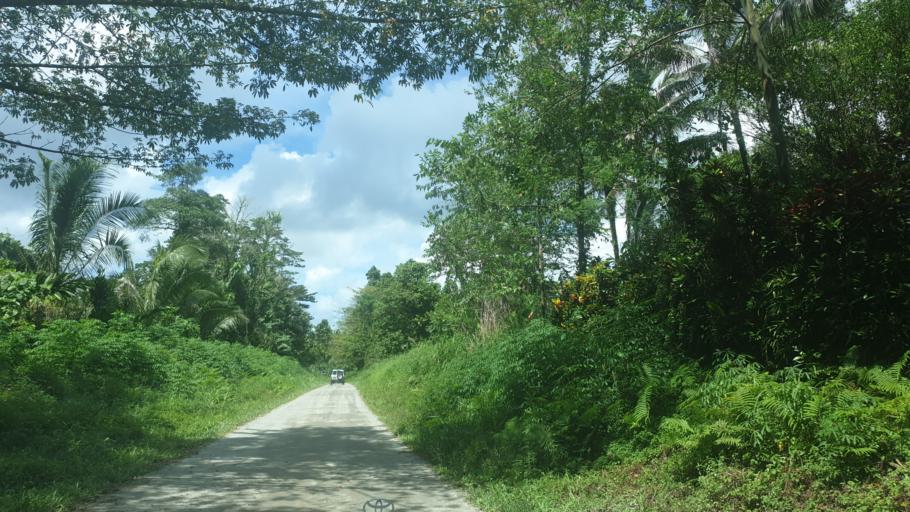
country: PG
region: Bougainville
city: Panguna
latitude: -6.7320
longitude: 155.4917
